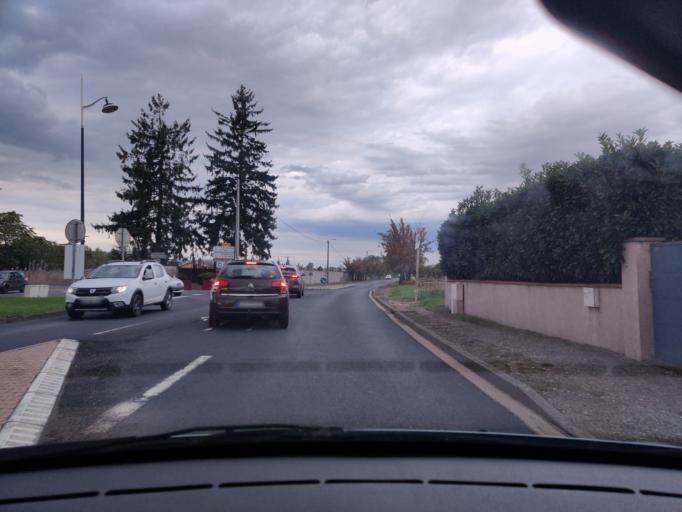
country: FR
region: Auvergne
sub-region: Departement du Puy-de-Dome
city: Saint-Bonnet-pres-Riom
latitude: 45.9315
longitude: 3.1116
